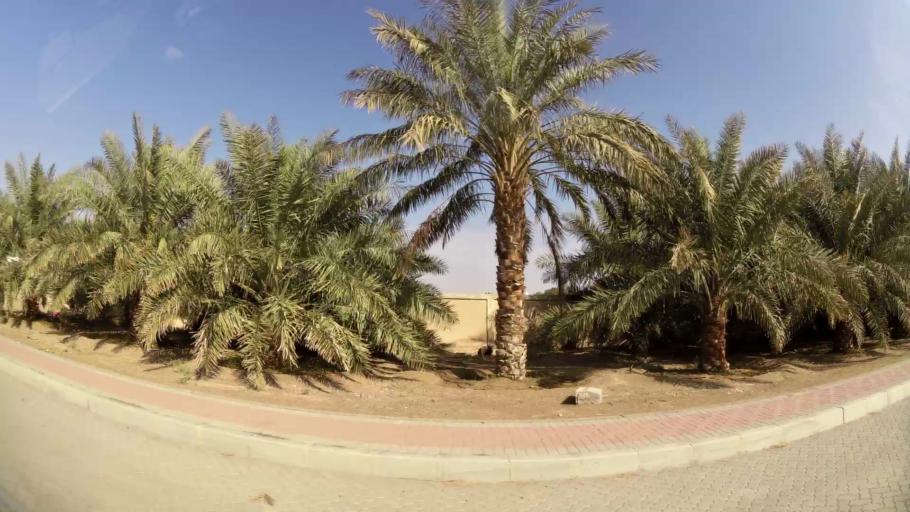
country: AE
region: Abu Dhabi
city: Al Ain
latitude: 24.0896
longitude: 55.9274
